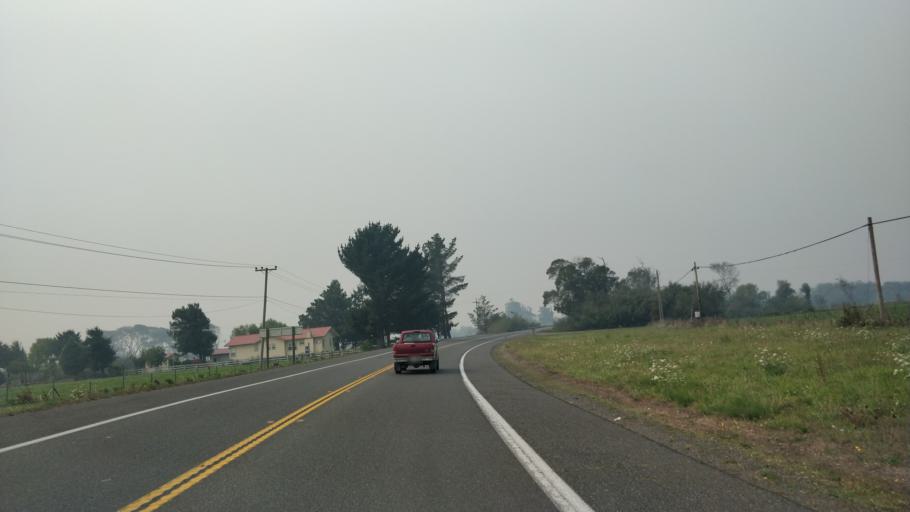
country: US
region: California
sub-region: Humboldt County
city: Ferndale
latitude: 40.5955
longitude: -124.2378
